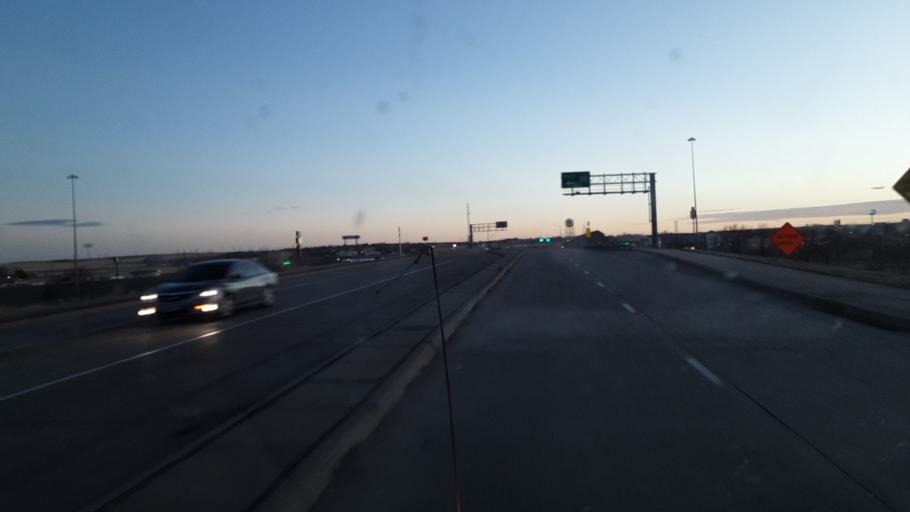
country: US
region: Nebraska
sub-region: Keith County
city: Ogallala
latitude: 41.1165
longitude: -101.7149
